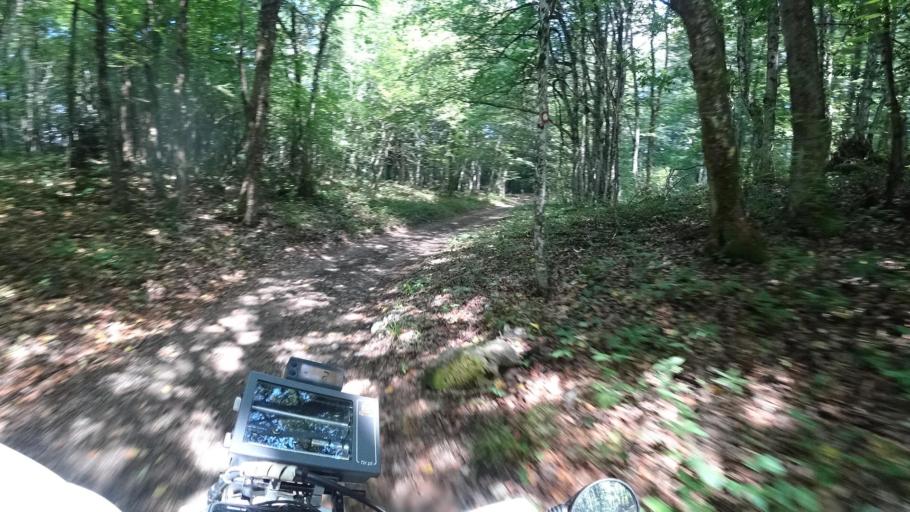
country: HR
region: Karlovacka
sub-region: Grad Ogulin
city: Ogulin
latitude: 45.2497
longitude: 15.1871
